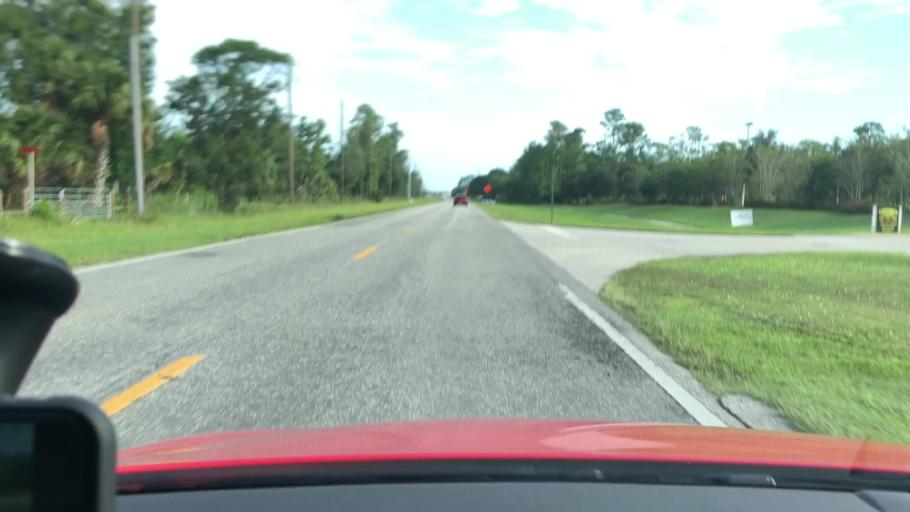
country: US
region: Florida
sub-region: Volusia County
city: Daytona Beach
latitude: 29.1762
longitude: -81.0904
